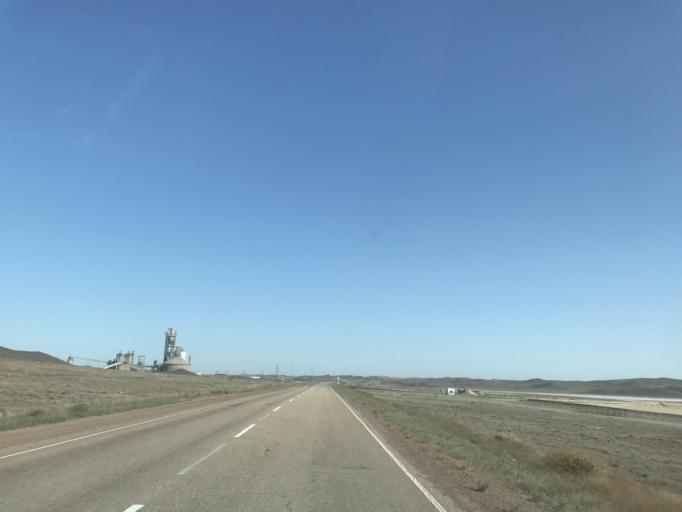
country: KZ
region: Zhambyl
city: Mynaral
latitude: 45.3972
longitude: 73.6414
